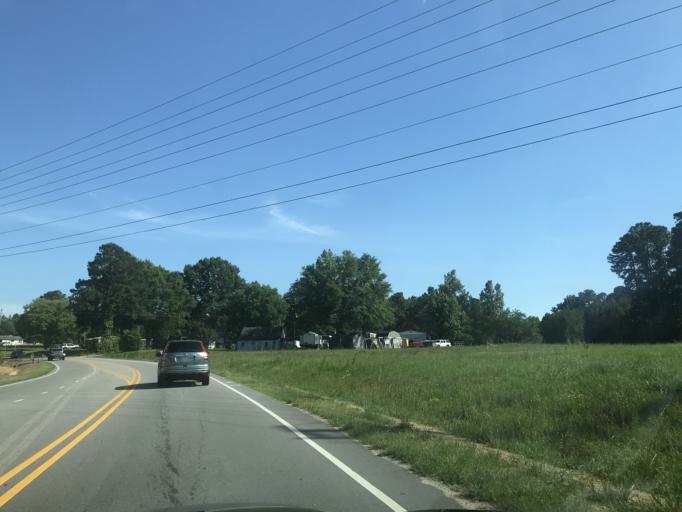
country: US
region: North Carolina
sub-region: Wake County
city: Garner
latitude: 35.6702
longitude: -78.5751
